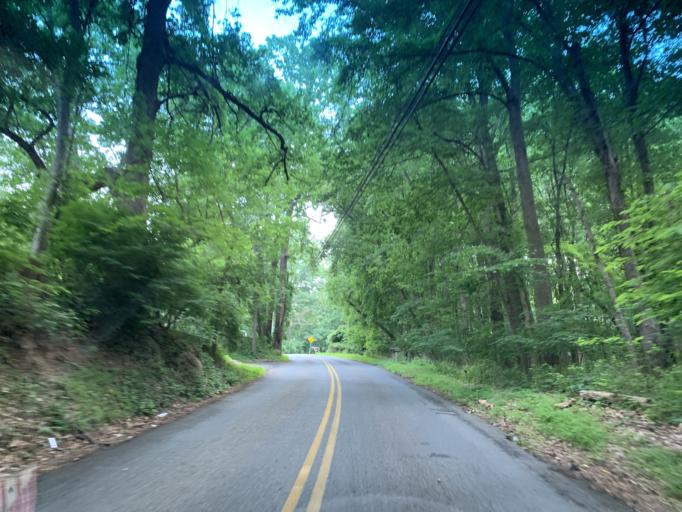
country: US
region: Maryland
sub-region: Harford County
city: Fallston
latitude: 39.5302
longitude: -76.4130
